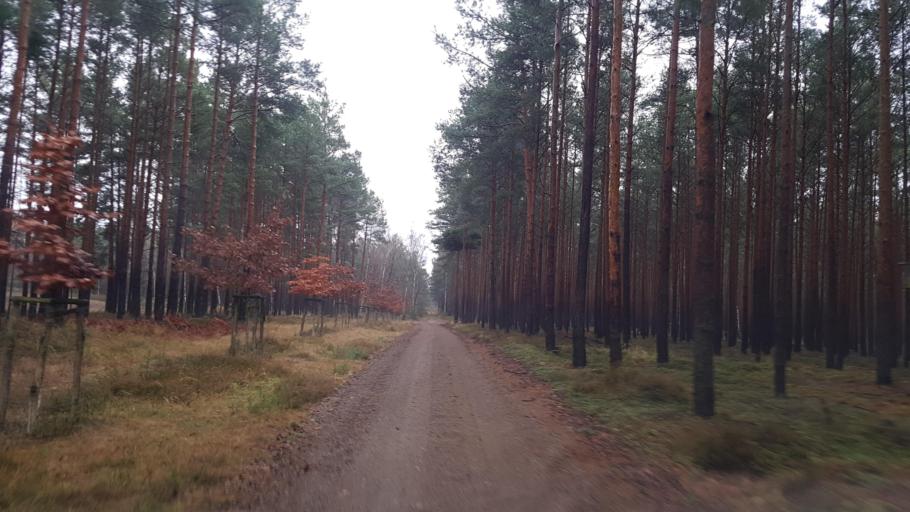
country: DE
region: Brandenburg
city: Grossraschen
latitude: 51.6306
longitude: 13.9675
